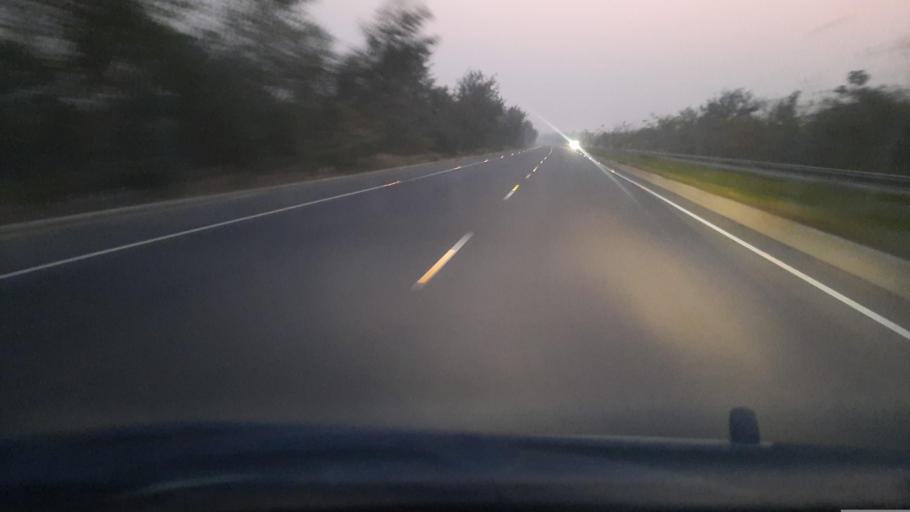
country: BD
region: Dhaka
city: Char Bhadrasan
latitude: 23.3984
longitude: 90.2226
